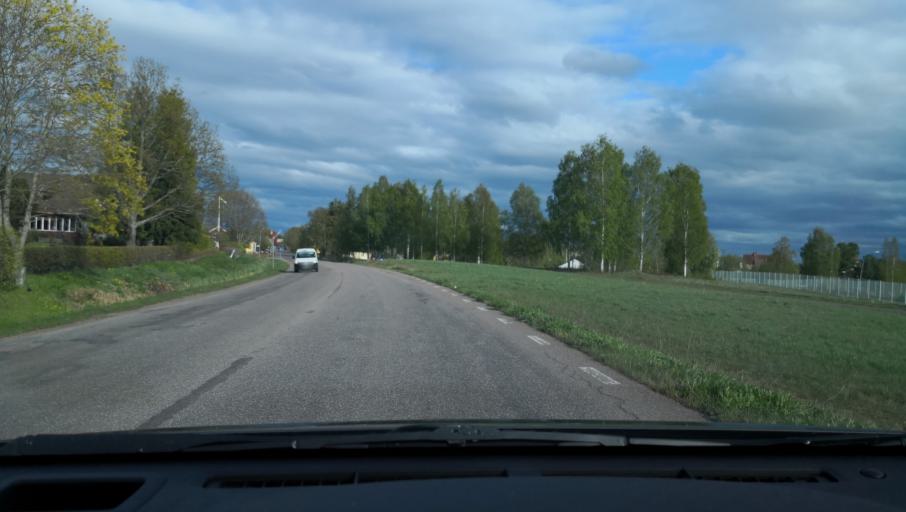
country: SE
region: Dalarna
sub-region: Hedemora Kommun
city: Hedemora
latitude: 60.2798
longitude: 15.9692
